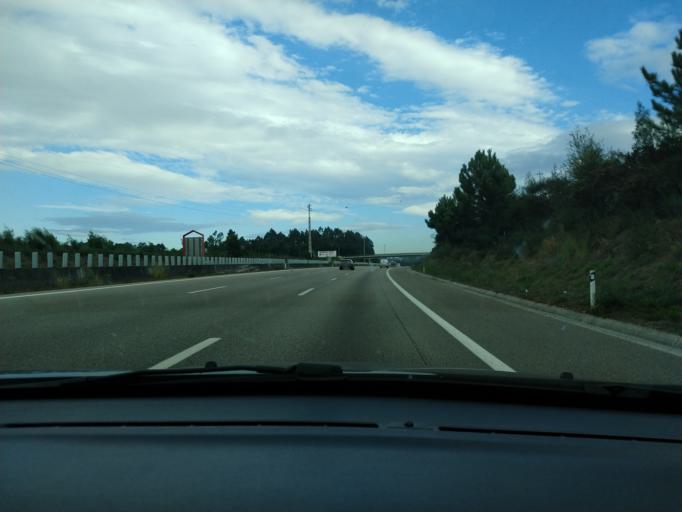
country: PT
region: Aveiro
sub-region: Santa Maria da Feira
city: Rio Meao
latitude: 40.9445
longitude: -8.5741
